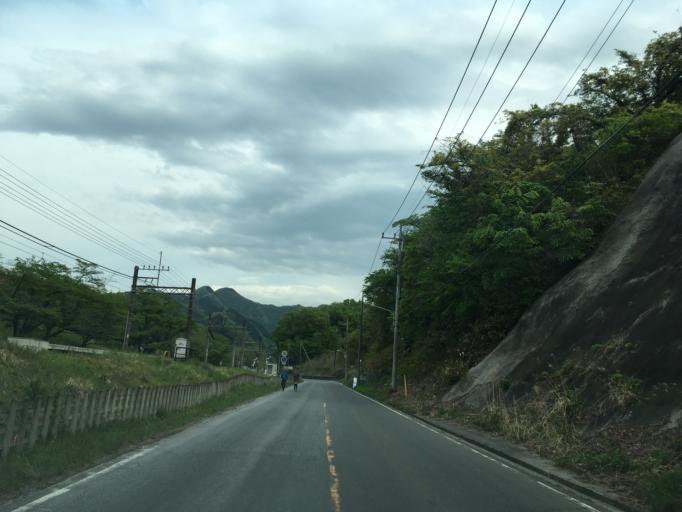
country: JP
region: Saitama
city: Chichibu
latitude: 35.9787
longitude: 139.1028
